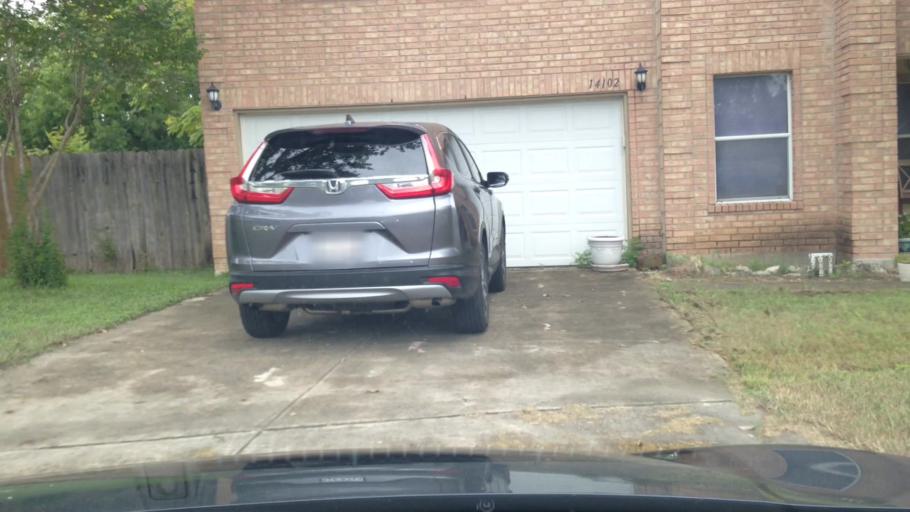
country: US
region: Texas
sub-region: Bexar County
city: Windcrest
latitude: 29.5707
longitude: -98.4145
